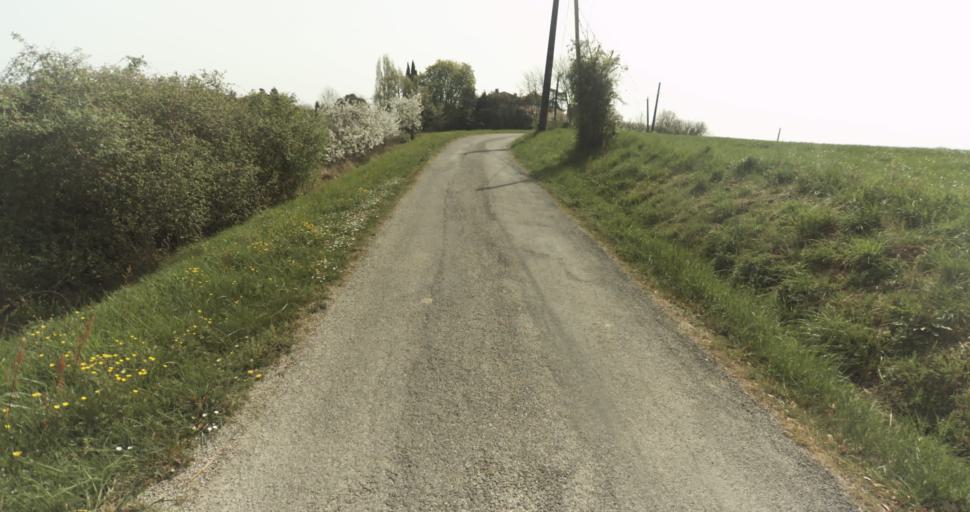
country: FR
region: Midi-Pyrenees
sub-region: Departement du Tarn-et-Garonne
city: Moissac
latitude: 44.1142
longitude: 1.0653
